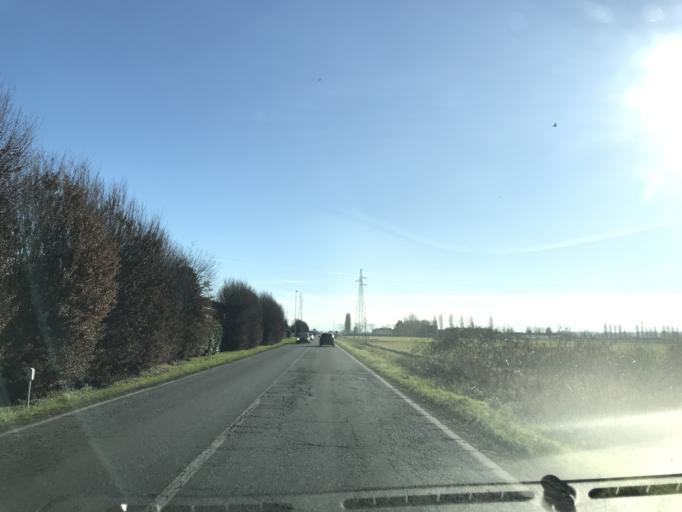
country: IT
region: Lombardy
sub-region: Provincia di Lodi
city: Ossago Lodigiano
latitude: 45.2434
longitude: 9.5353
